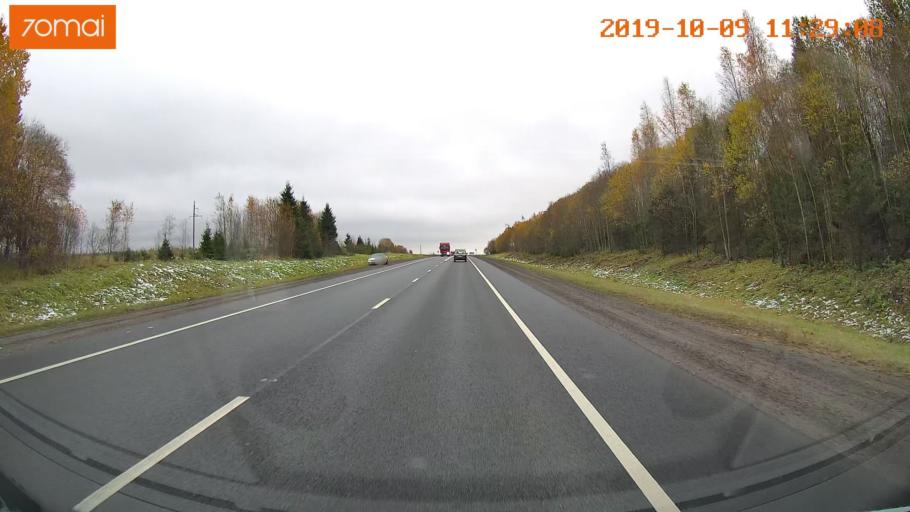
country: RU
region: Vologda
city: Vologda
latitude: 59.0641
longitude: 40.0487
